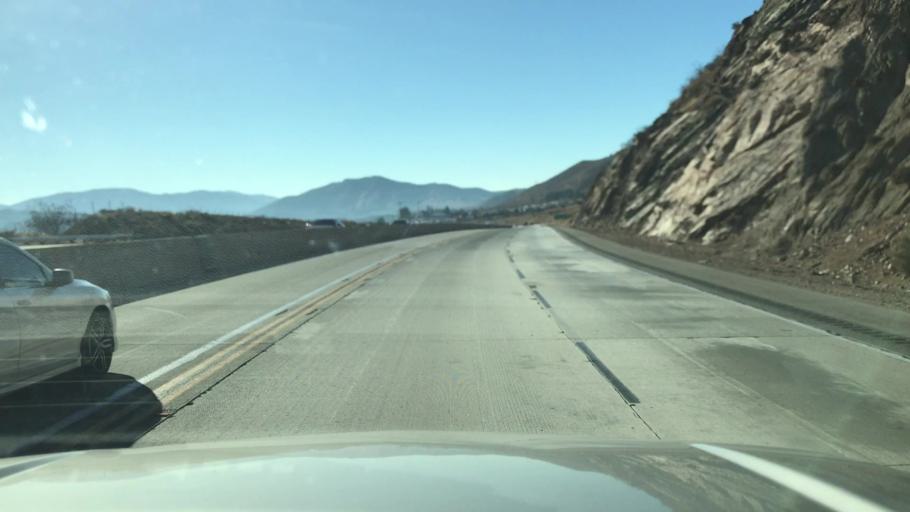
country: US
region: California
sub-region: Los Angeles County
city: Vincent
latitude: 34.4917
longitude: -118.1298
